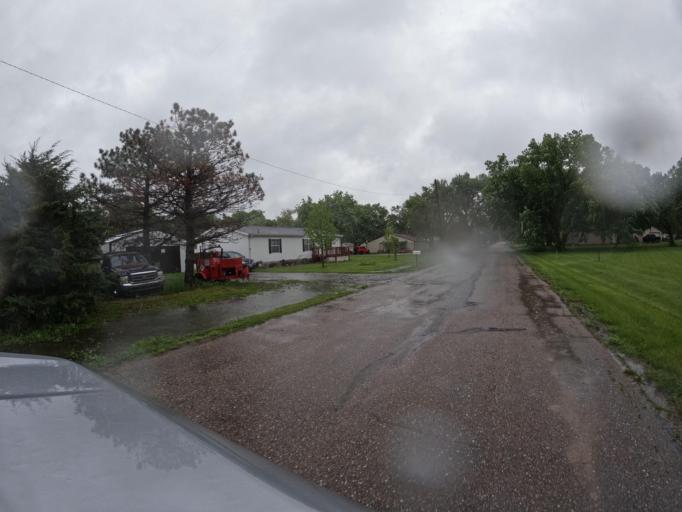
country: US
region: Nebraska
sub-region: Gage County
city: Wymore
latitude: 40.1218
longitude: -96.6754
